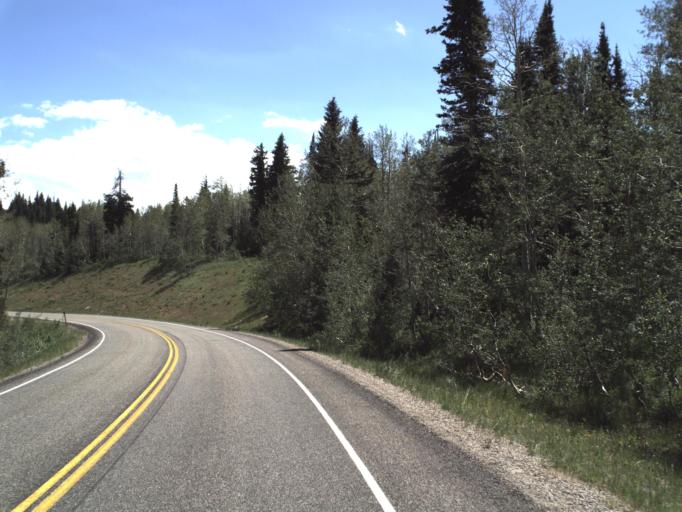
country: US
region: Utah
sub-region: Weber County
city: Wolf Creek
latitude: 41.4616
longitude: -111.5007
